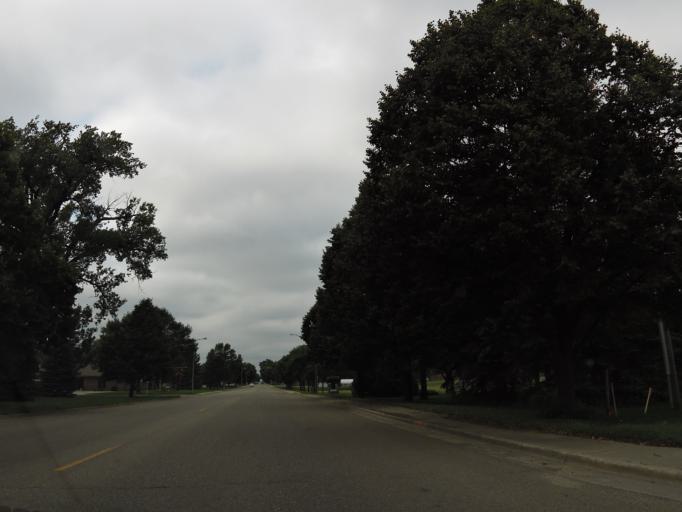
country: US
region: Minnesota
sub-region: Renville County
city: Renville
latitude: 44.7893
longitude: -95.2035
